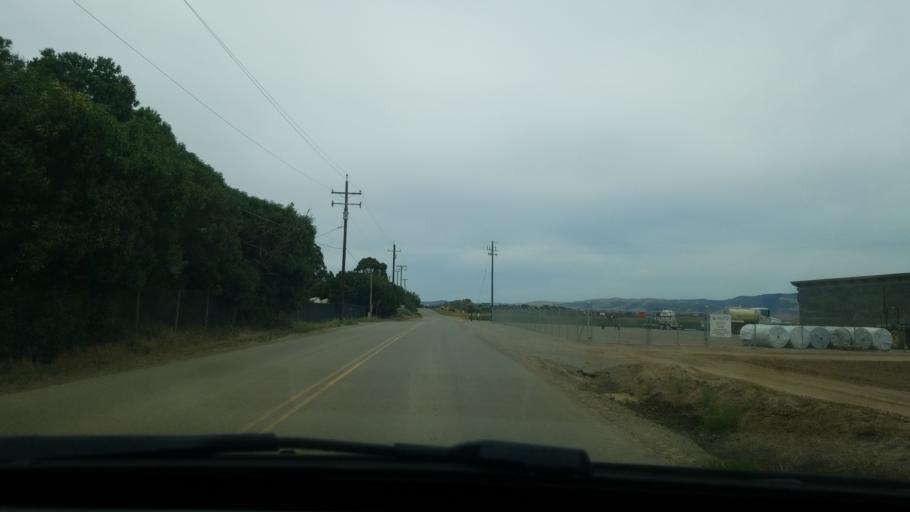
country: US
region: California
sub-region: Santa Barbara County
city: Guadalupe
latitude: 34.9903
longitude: -120.5140
